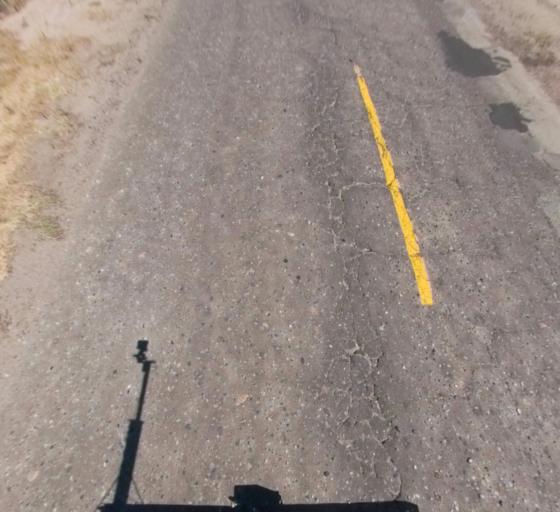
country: US
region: California
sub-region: Madera County
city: Parkwood
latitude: 36.8713
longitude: -120.0014
